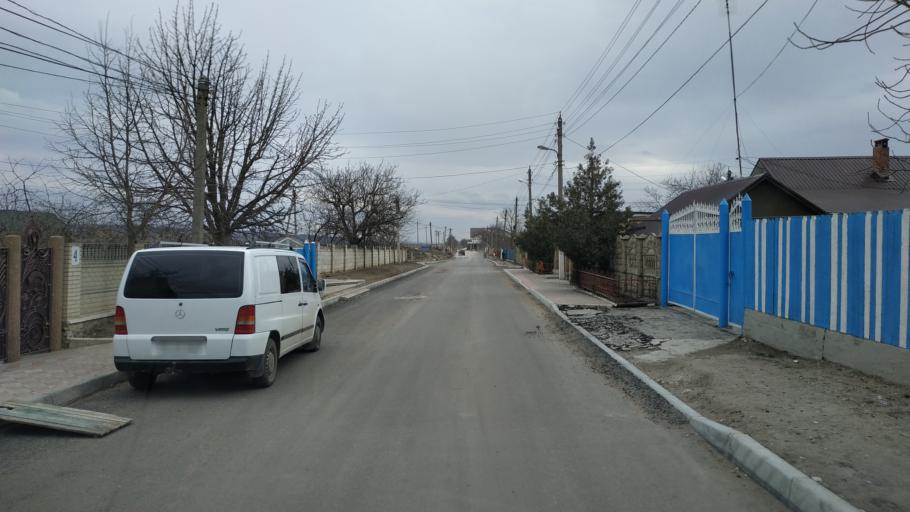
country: MD
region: Laloveni
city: Ialoveni
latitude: 46.8602
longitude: 28.7850
